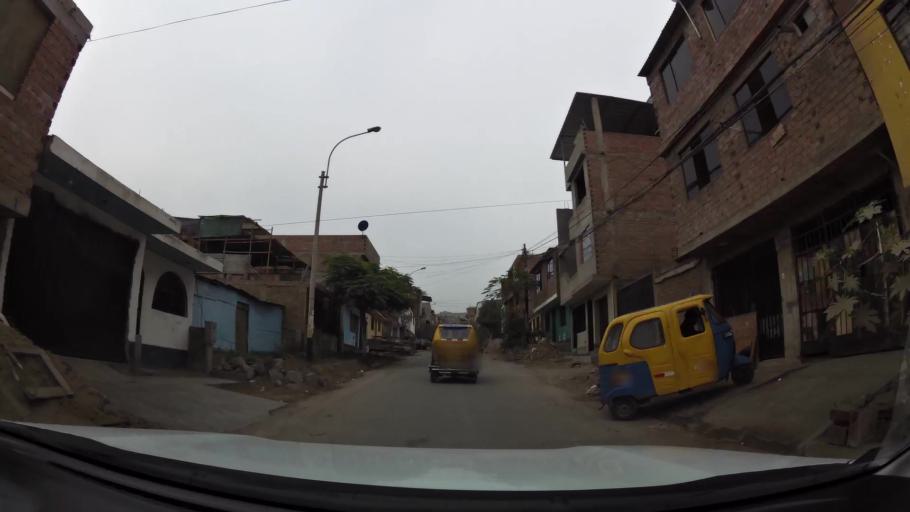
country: PE
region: Lima
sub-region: Lima
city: Surco
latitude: -12.1755
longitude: -76.9647
